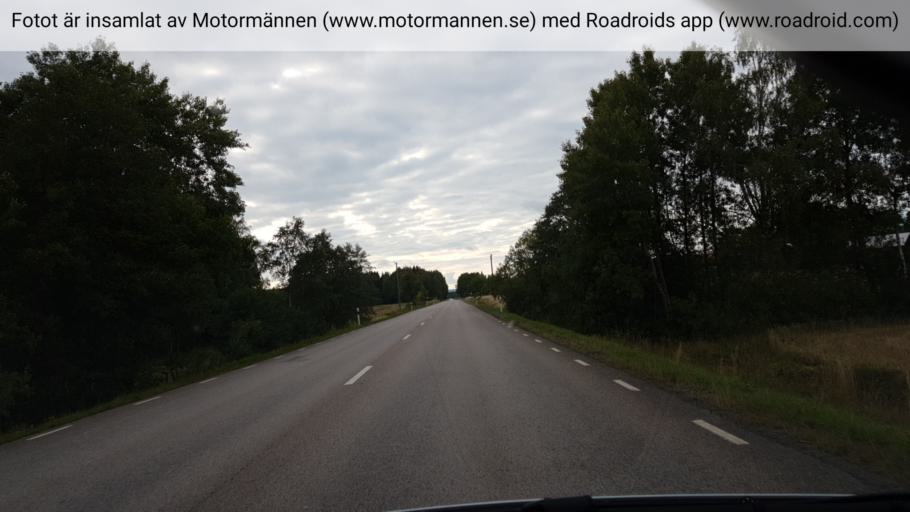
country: SE
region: Vaestra Goetaland
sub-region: Tidaholms Kommun
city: Olofstorp
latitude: 58.3656
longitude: 14.0196
